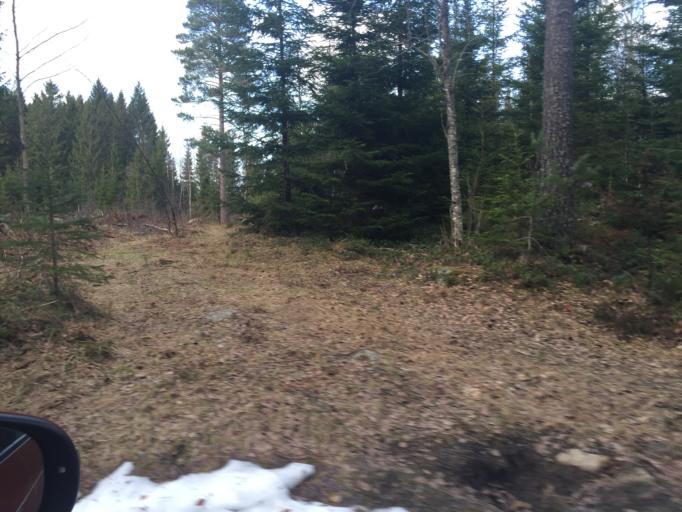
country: SE
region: Soedermanland
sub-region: Vingakers Kommun
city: Vingaker
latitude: 58.9934
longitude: 15.6816
